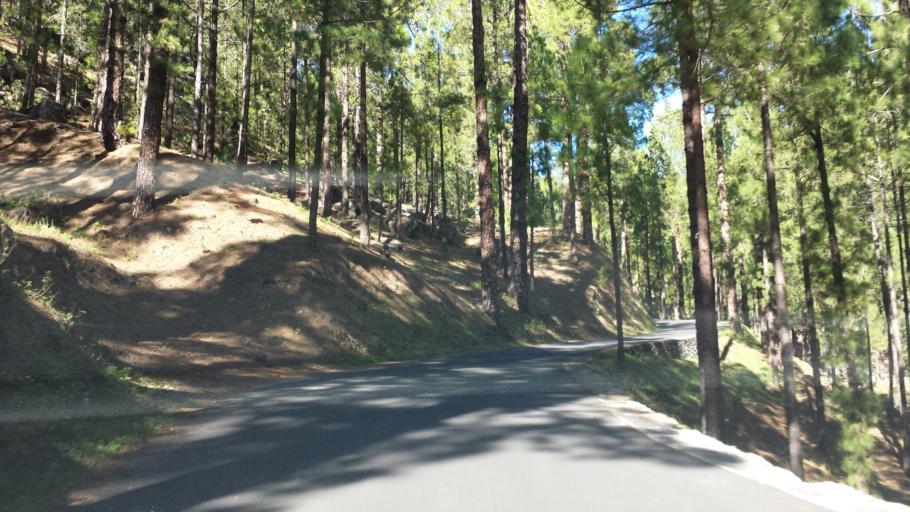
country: ES
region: Canary Islands
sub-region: Provincia de Santa Cruz de Tenerife
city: El Paso
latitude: 28.6920
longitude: -17.8519
